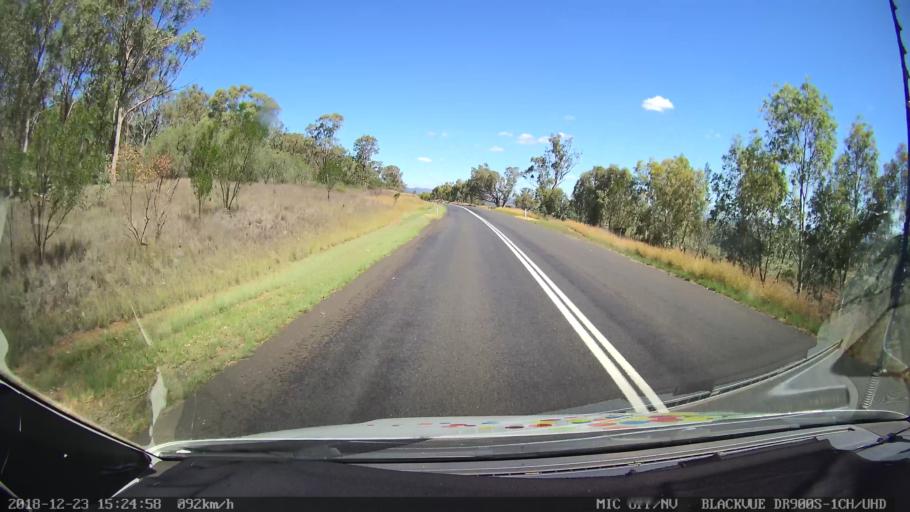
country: AU
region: New South Wales
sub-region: Tamworth Municipality
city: Manilla
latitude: -30.8987
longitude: 150.8262
